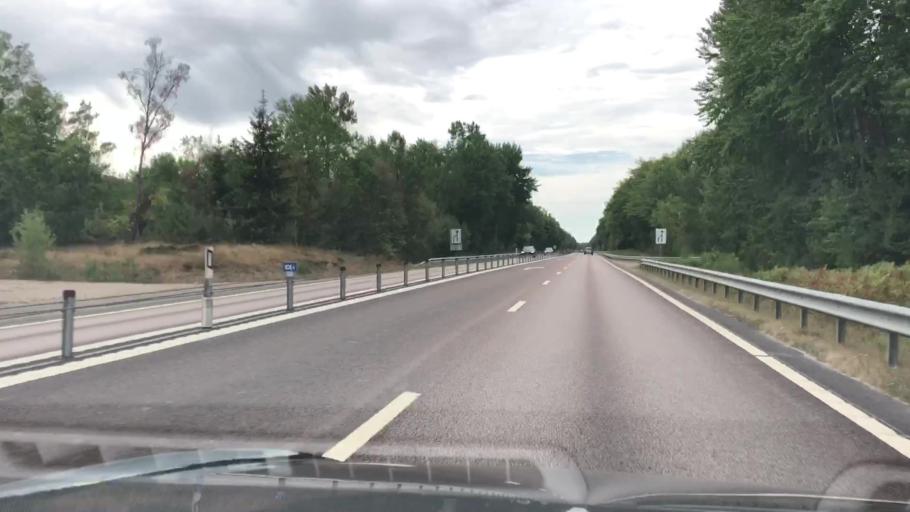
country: SE
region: Blekinge
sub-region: Karlskrona Kommun
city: Jaemjoe
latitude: 56.2404
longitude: 15.9278
